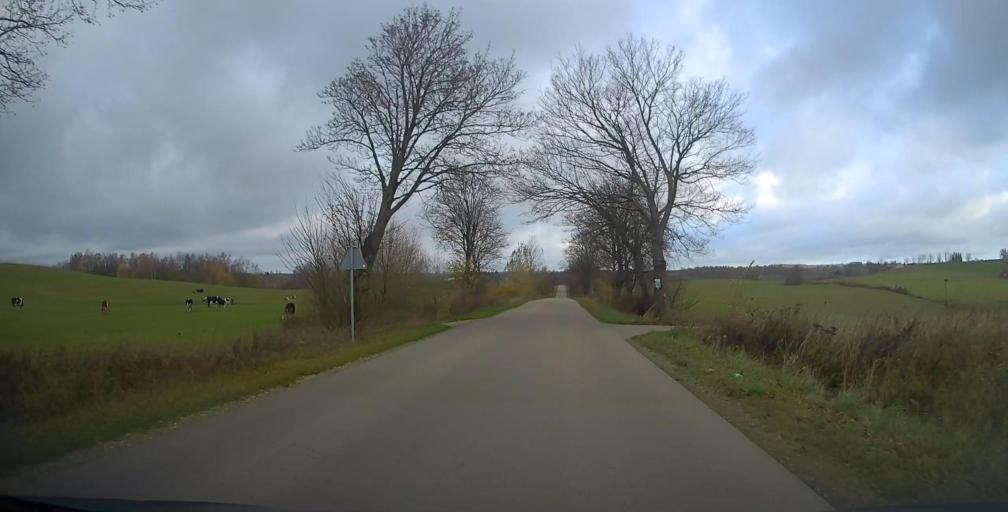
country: PL
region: Podlasie
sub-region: Suwalki
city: Suwalki
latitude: 54.3189
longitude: 22.8634
